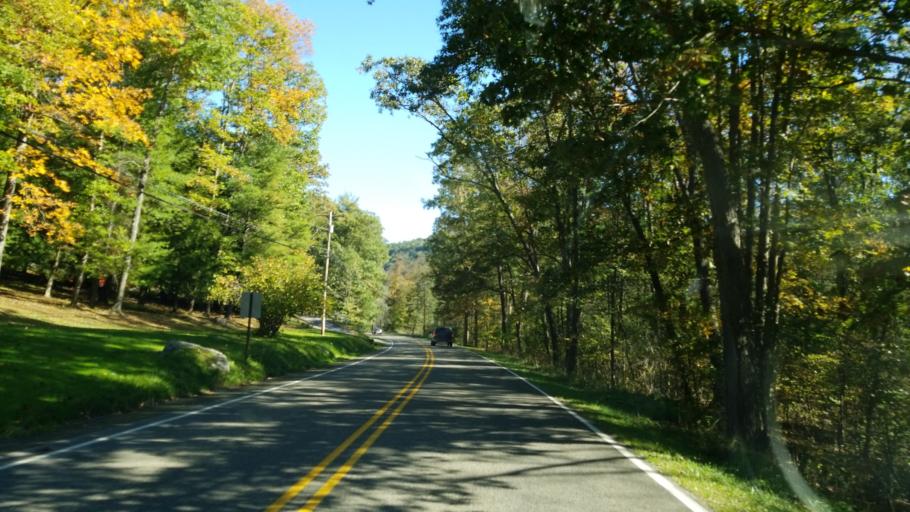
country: US
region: Pennsylvania
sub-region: Elk County
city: Saint Marys
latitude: 41.2820
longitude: -78.4517
